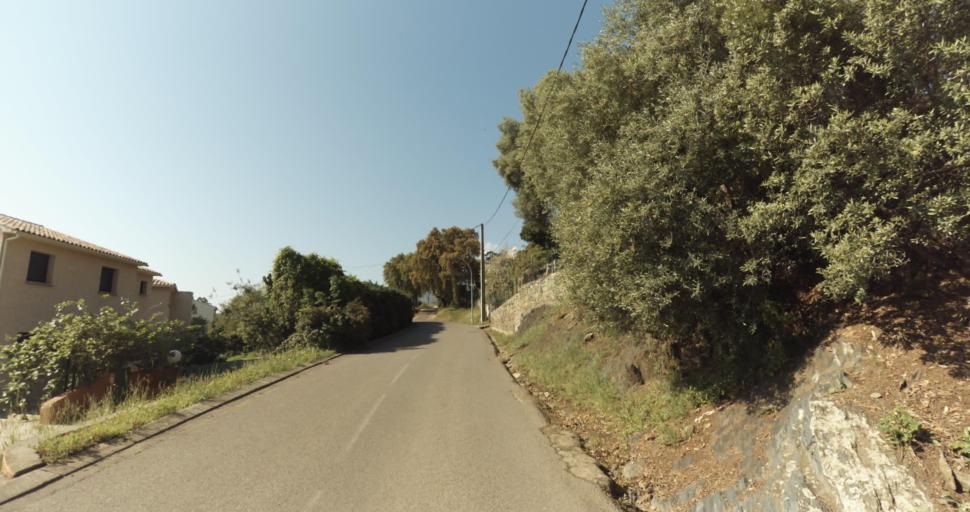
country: FR
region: Corsica
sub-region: Departement de la Haute-Corse
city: Biguglia
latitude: 42.6269
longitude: 9.4223
